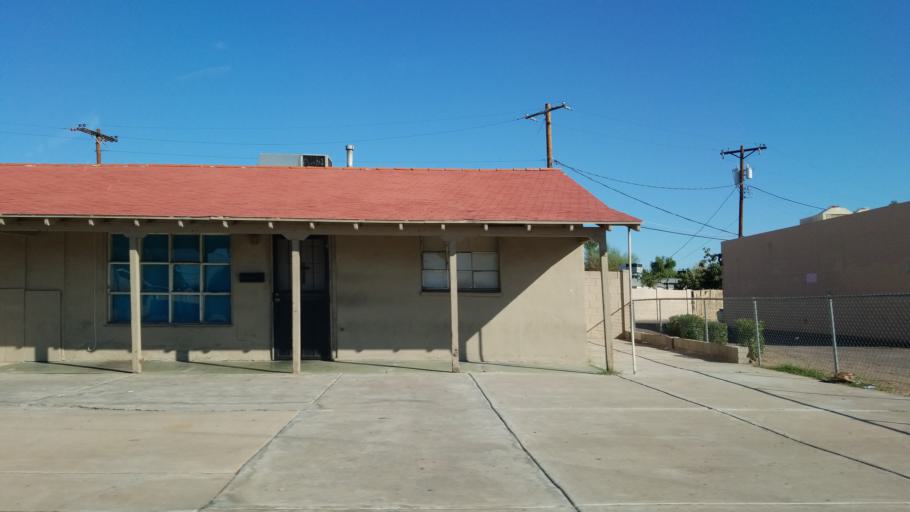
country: US
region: Arizona
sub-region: Maricopa County
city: Glendale
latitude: 33.5241
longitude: -112.1181
